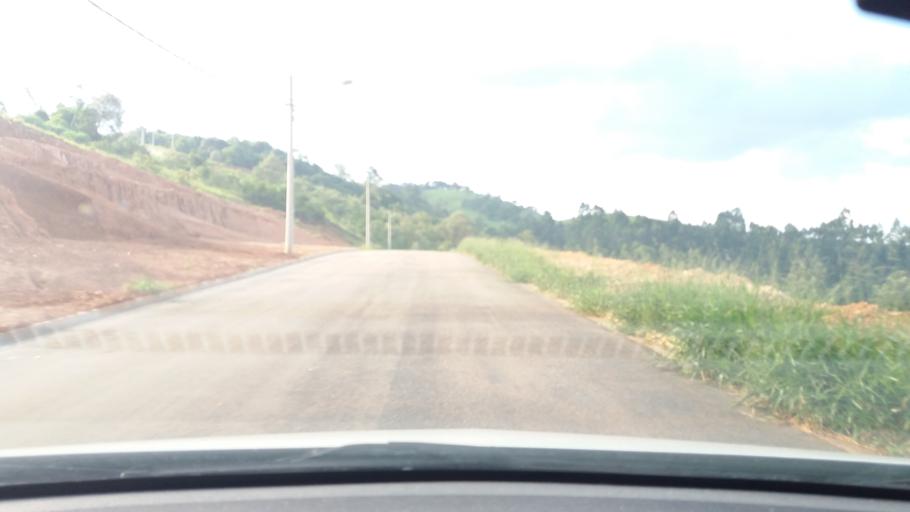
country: BR
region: Sao Paulo
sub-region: Bom Jesus Dos Perdoes
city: Bom Jesus dos Perdoes
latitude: -23.1530
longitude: -46.4751
